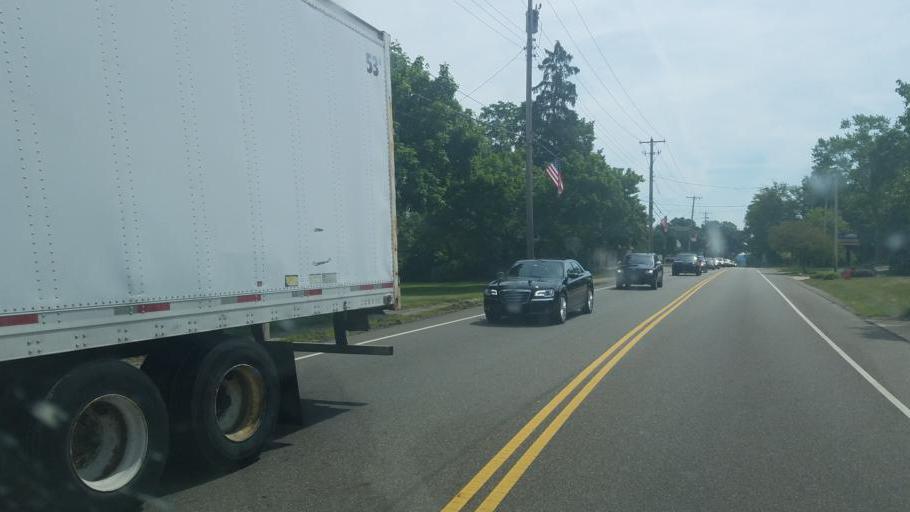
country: US
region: Ohio
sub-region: Summit County
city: Macedonia
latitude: 41.3142
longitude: -81.5378
